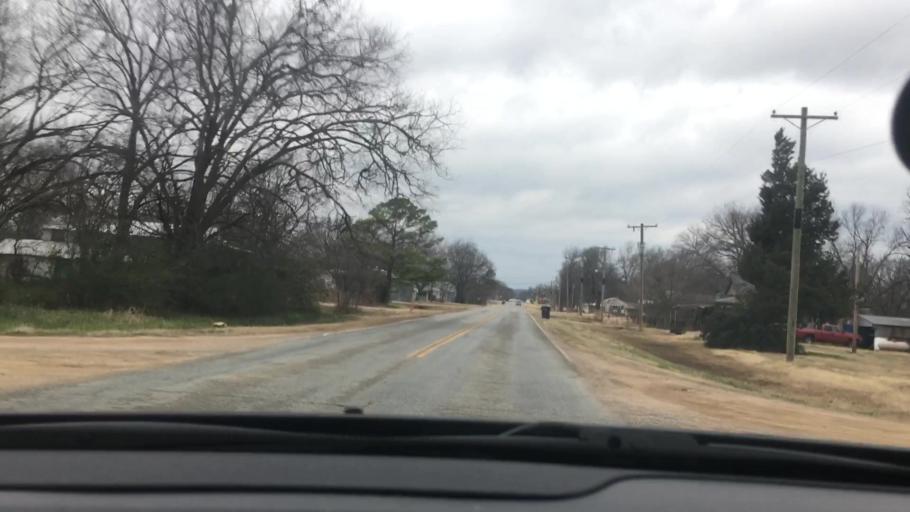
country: US
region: Oklahoma
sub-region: Coal County
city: Coalgate
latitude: 34.3750
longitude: -96.4184
